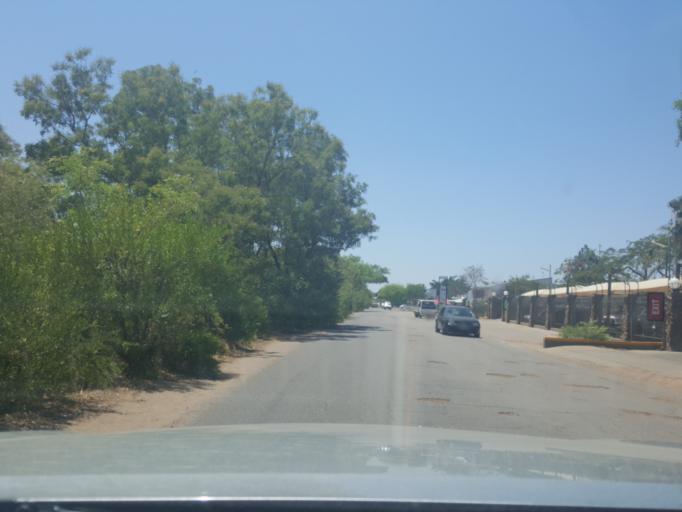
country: BW
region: South East
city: Gaborone
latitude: -24.6815
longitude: 25.8919
